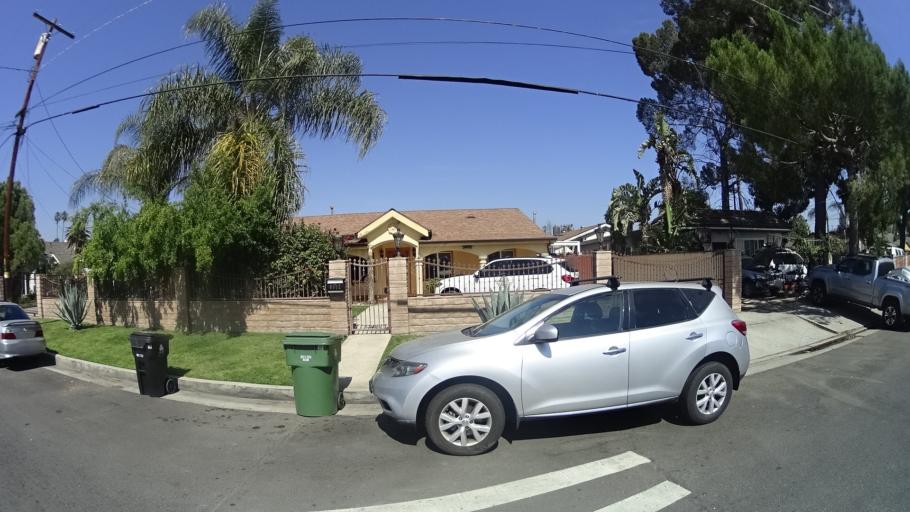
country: US
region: California
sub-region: Los Angeles County
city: Van Nuys
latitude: 34.1961
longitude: -118.4214
